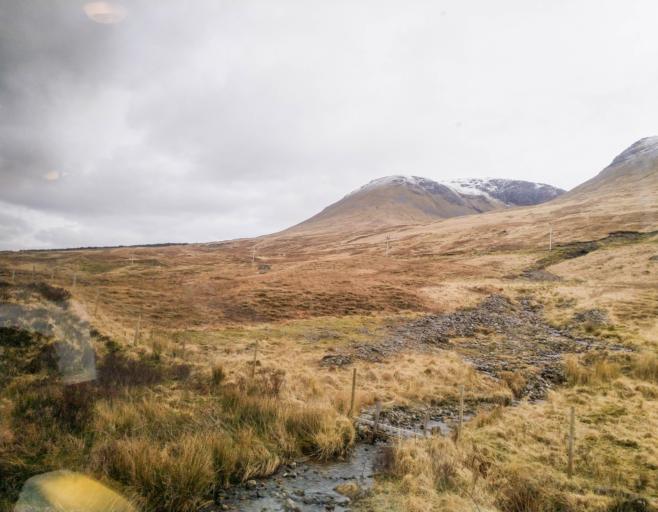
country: GB
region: Scotland
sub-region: Highland
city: Spean Bridge
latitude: 56.5104
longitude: -4.7602
